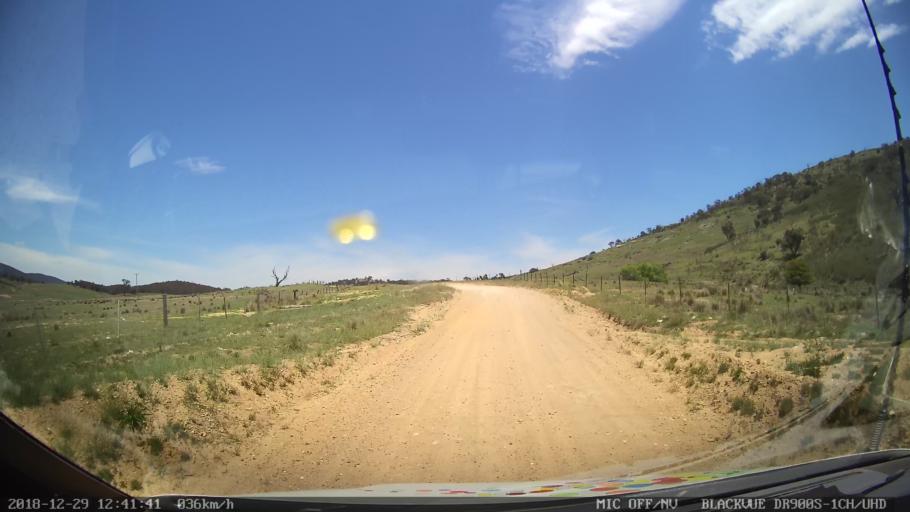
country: AU
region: Australian Capital Territory
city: Macarthur
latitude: -35.6090
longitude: 149.2216
